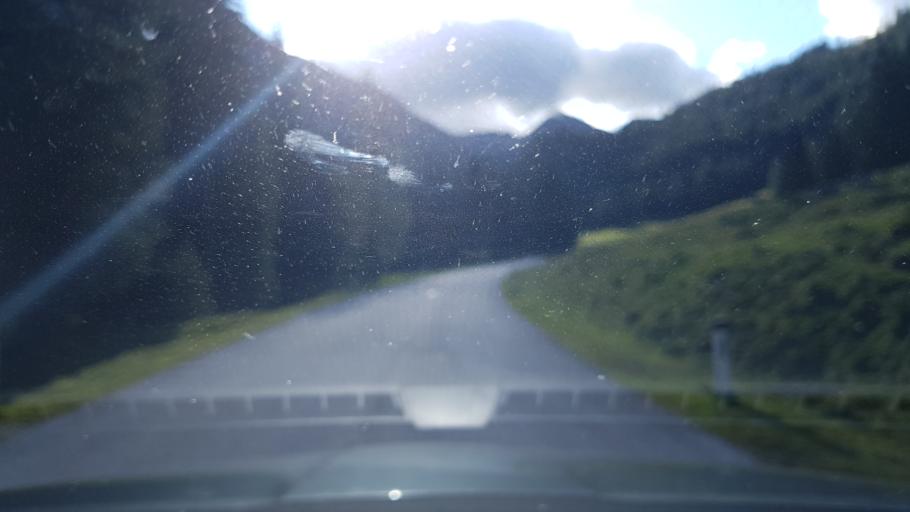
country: AT
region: Styria
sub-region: Politischer Bezirk Liezen
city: Sankt Nikolai im Solktal
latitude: 47.3017
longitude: 14.0671
